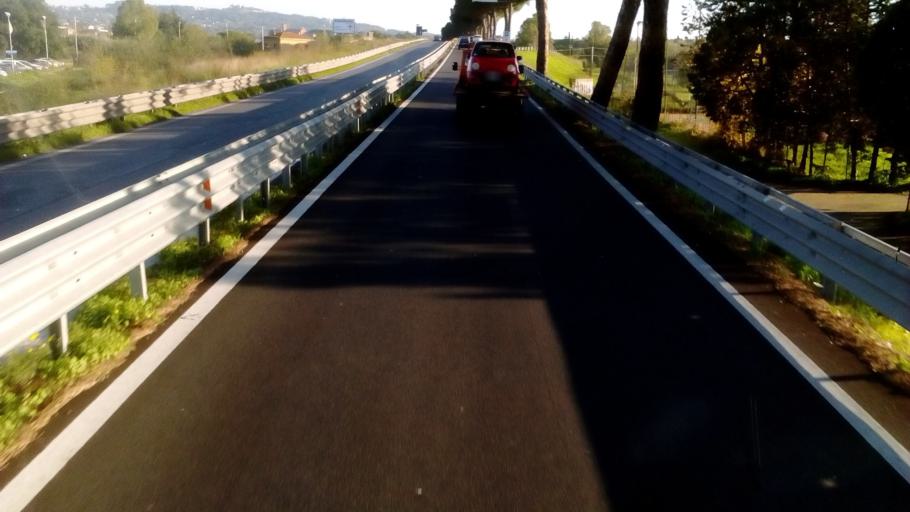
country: IT
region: Latium
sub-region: Citta metropolitana di Roma Capitale
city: Ciampino
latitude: 41.7792
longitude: 12.6048
